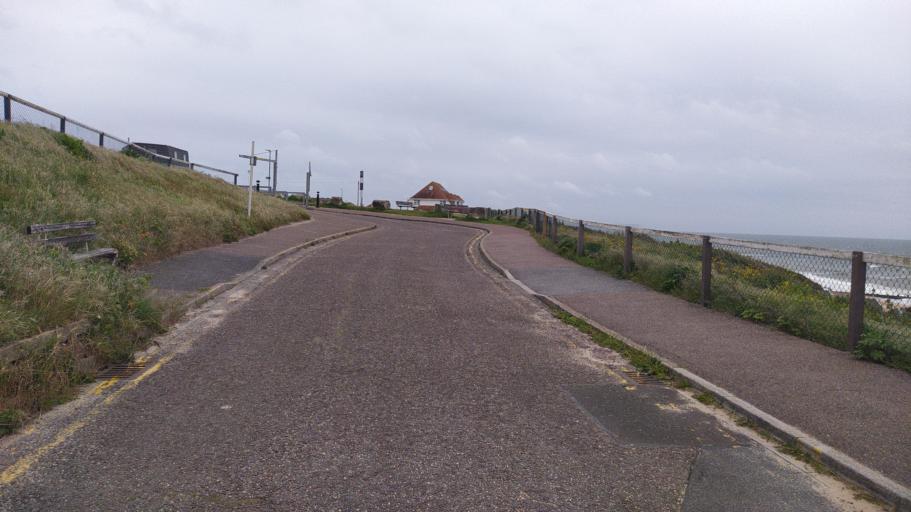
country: GB
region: England
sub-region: Dorset
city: Christchurch
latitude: 50.7195
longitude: -1.7916
